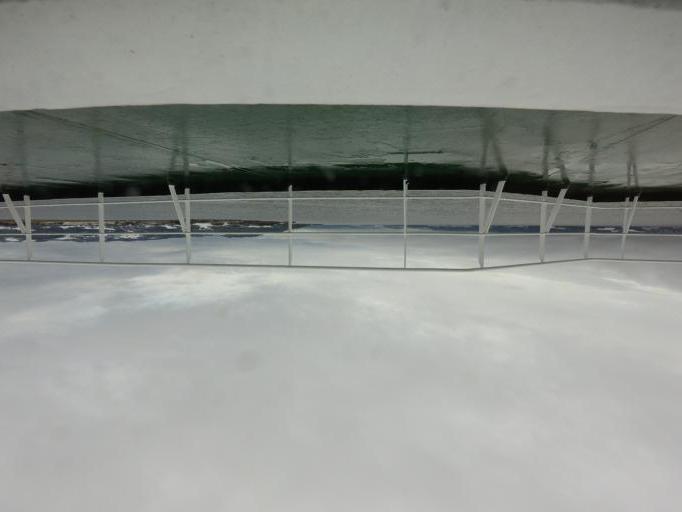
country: NO
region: Sor-Trondelag
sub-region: Rissa
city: Rissa
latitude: 63.4785
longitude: 10.0170
